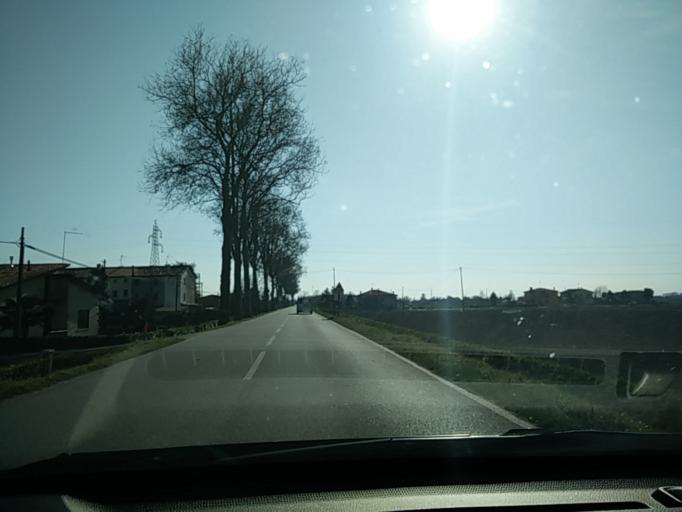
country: IT
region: Veneto
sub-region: Provincia di Venezia
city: Musile di Piave
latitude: 45.5989
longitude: 12.5590
